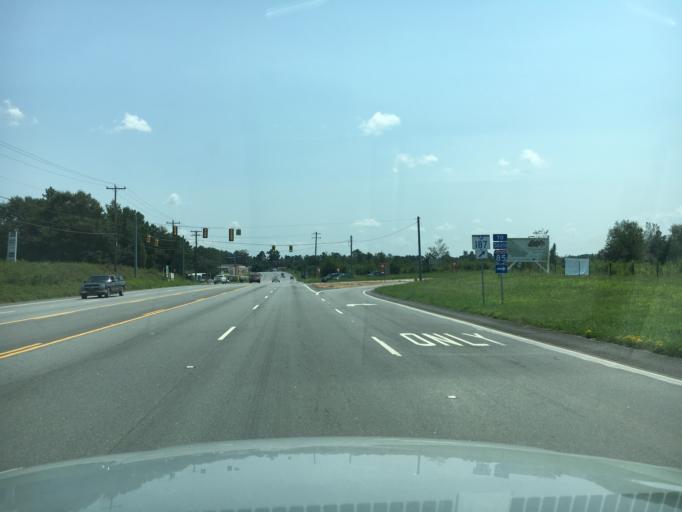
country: US
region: South Carolina
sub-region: Anderson County
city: Pendleton
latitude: 34.6261
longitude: -82.7797
